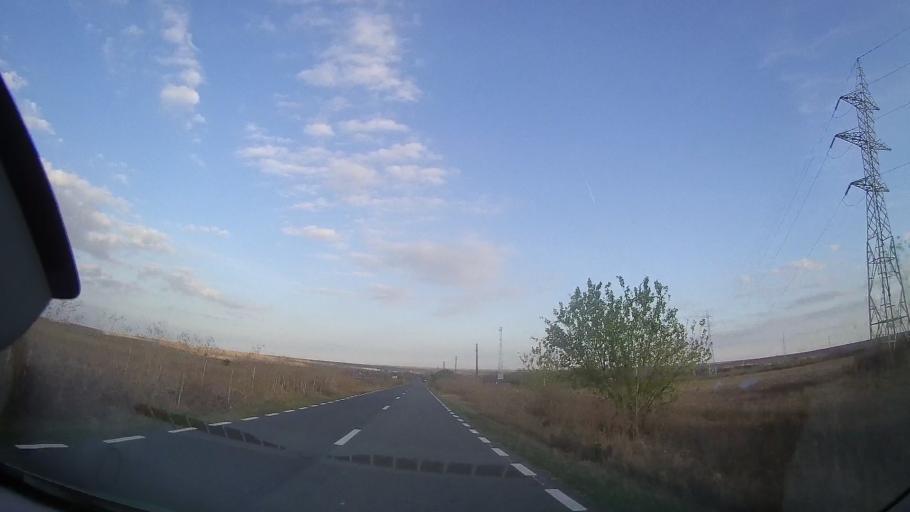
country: RO
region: Constanta
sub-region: Comuna Chirnogeni
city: Plopeni
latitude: 43.9514
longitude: 28.1722
